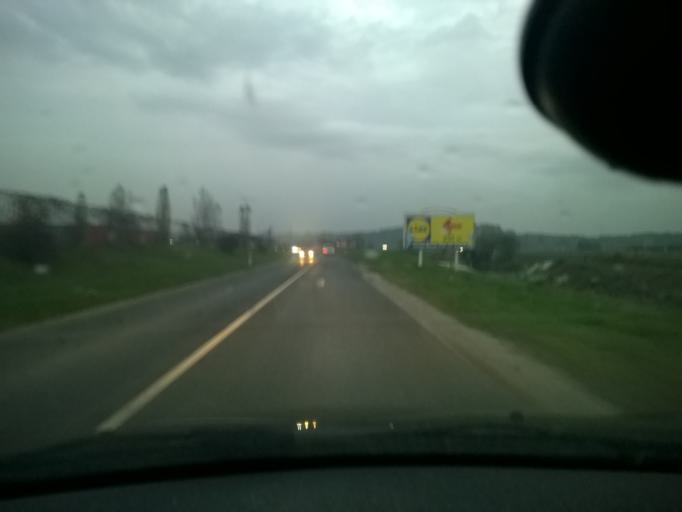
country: HR
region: Krapinsko-Zagorska
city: Zabok
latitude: 46.0204
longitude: 15.9043
